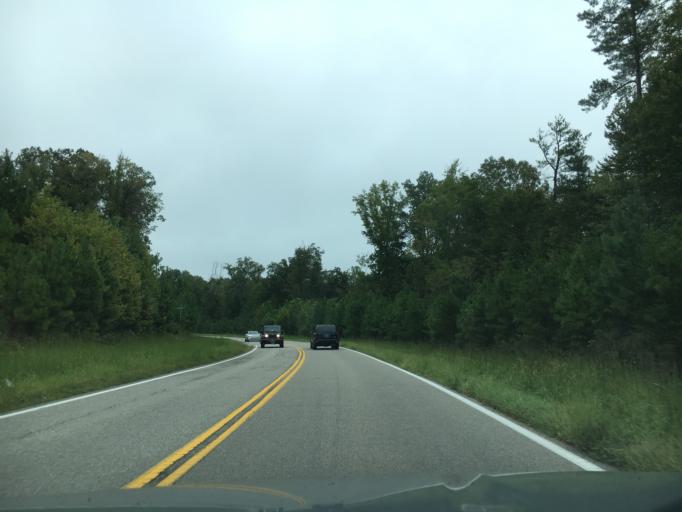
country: US
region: Virginia
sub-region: Chesterfield County
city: Woodlake
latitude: 37.5002
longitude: -77.7776
